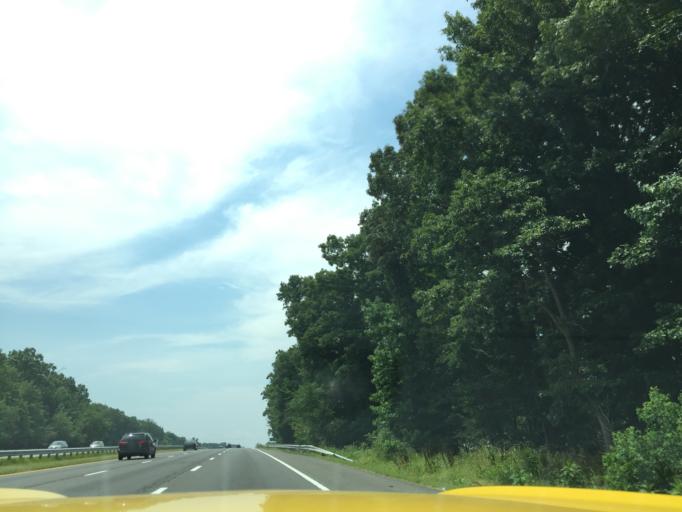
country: US
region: Maryland
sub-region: Prince George's County
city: Accokeek
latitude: 38.6782
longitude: -77.0033
